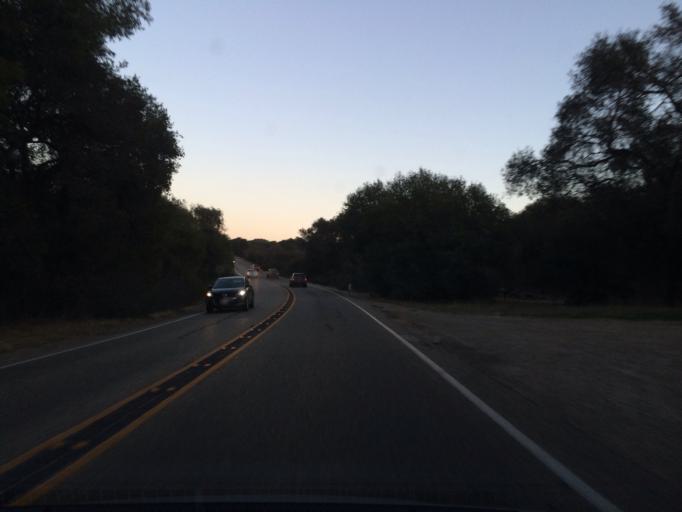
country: US
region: California
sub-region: Santa Barbara County
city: Santa Ynez
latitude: 34.5798
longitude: -119.9878
